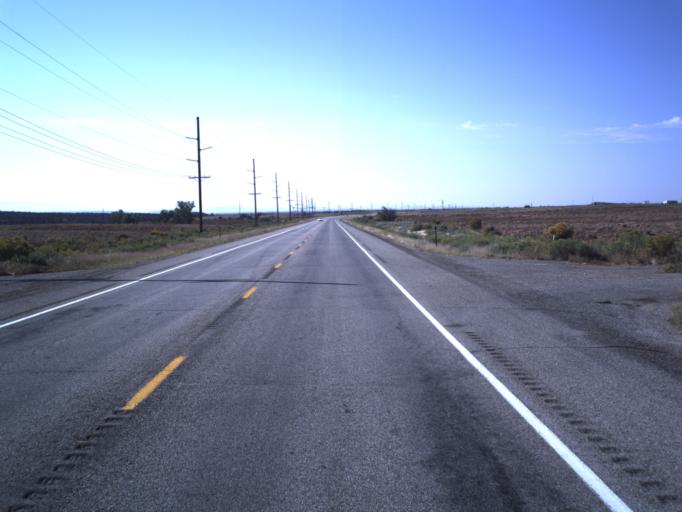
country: US
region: Utah
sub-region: San Juan County
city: Blanding
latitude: 37.5595
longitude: -109.4895
